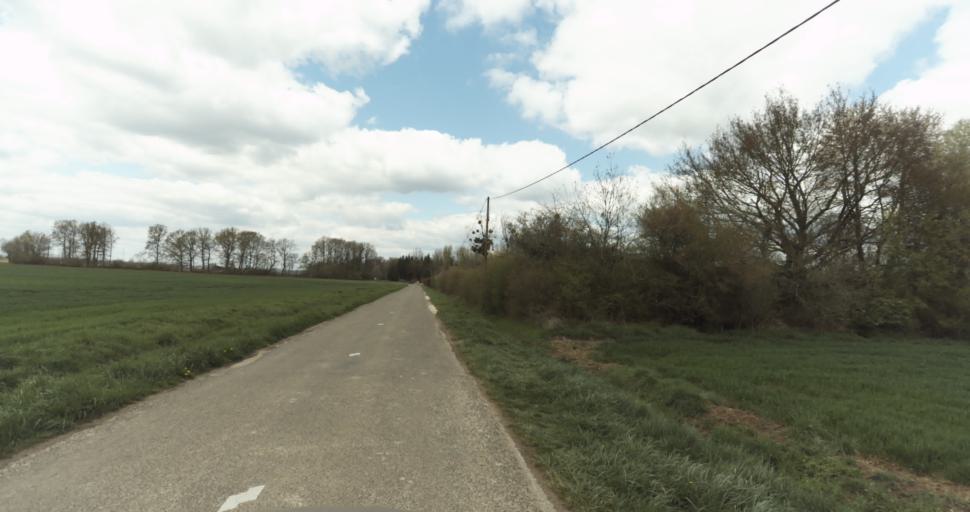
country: FR
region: Bourgogne
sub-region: Departement de la Cote-d'Or
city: Auxonne
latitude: 47.1789
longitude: 5.4201
